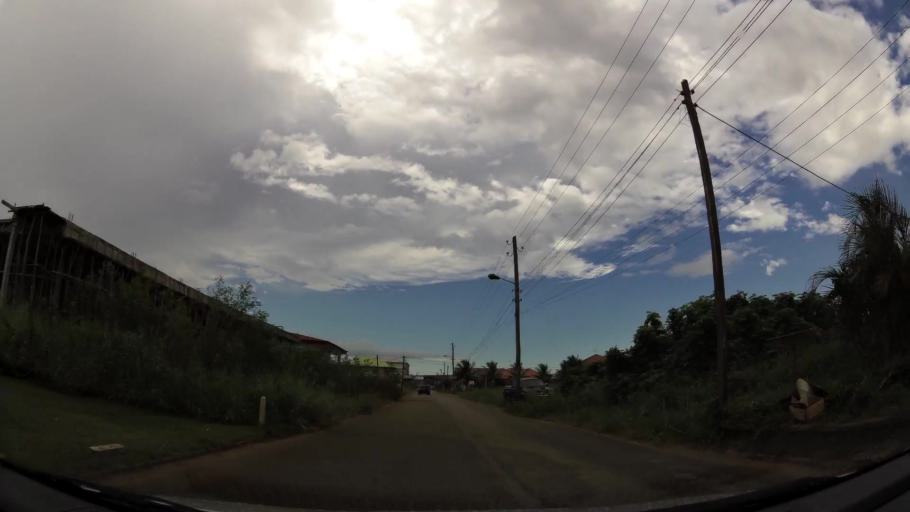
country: SR
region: Paramaribo
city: Paramaribo
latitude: 5.8619
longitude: -55.1236
